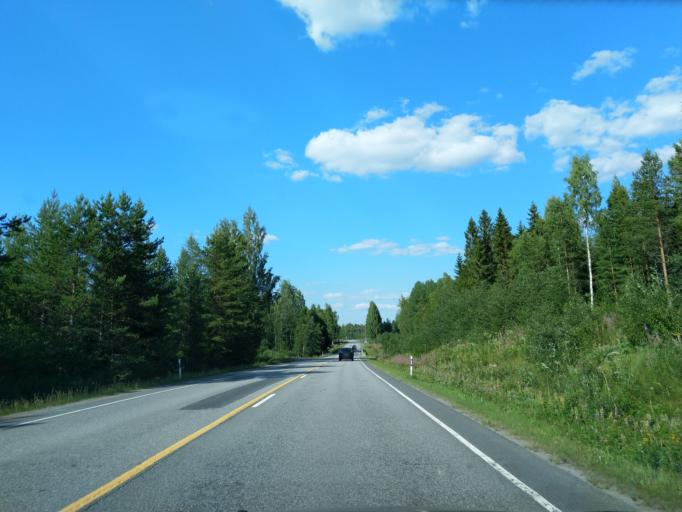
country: FI
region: Pirkanmaa
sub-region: Luoteis-Pirkanmaa
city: Kihnioe
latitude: 62.1719
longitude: 23.1647
